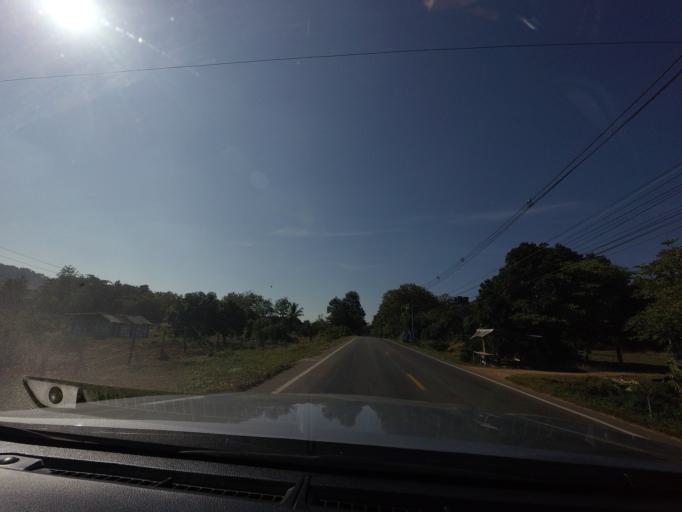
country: TH
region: Sukhothai
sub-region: Amphoe Si Satchanalai
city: Si Satchanalai
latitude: 17.6313
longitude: 99.6951
